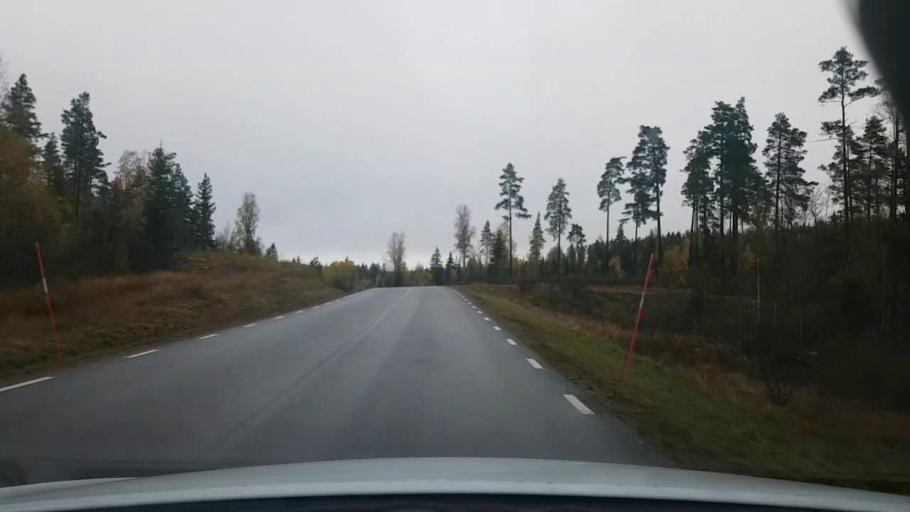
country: SE
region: Vaestra Goetaland
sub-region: Karlsborgs Kommun
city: Karlsborg
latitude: 58.6875
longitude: 14.5012
